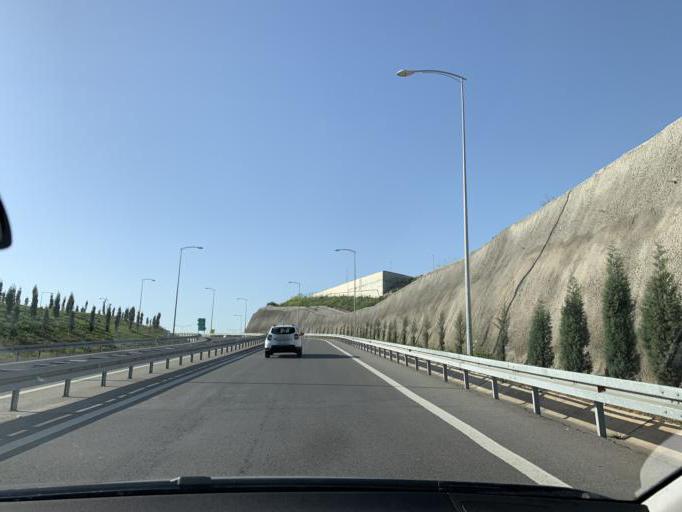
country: TR
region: Kocaeli
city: Tavsanli
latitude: 40.7755
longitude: 29.5197
